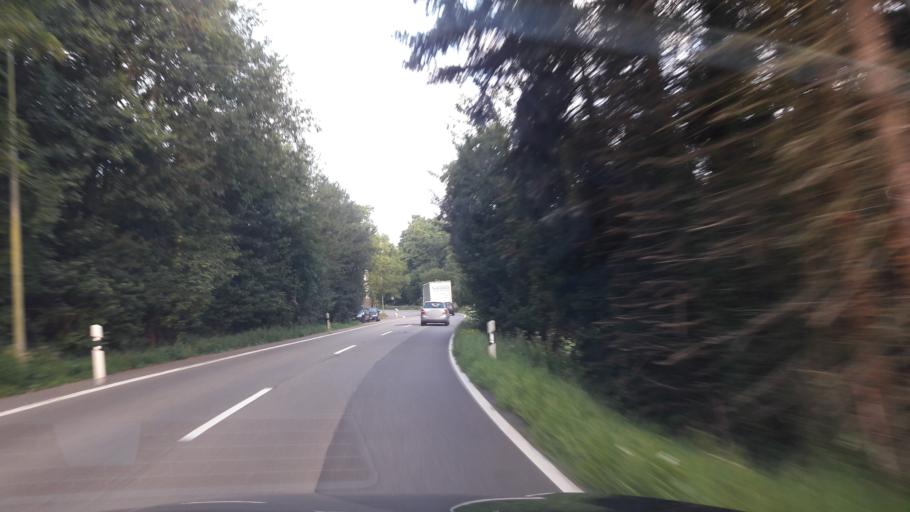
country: DE
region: Saarland
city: Sankt Ingbert
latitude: 49.1924
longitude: 7.1175
